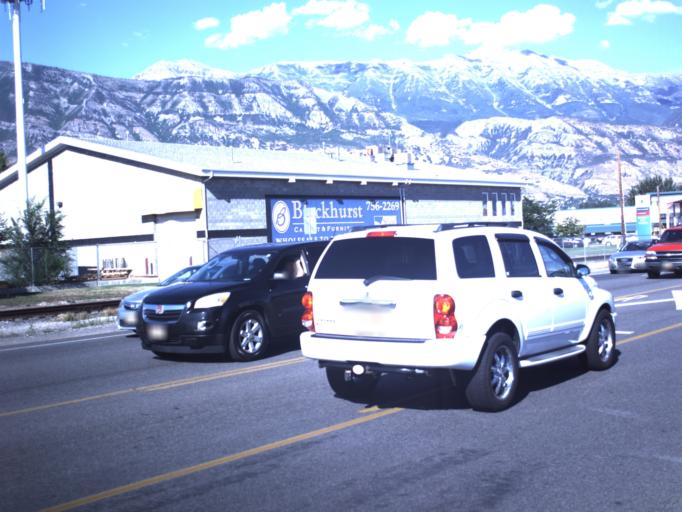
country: US
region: Utah
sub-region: Utah County
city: American Fork
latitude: 40.3704
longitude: -111.7707
